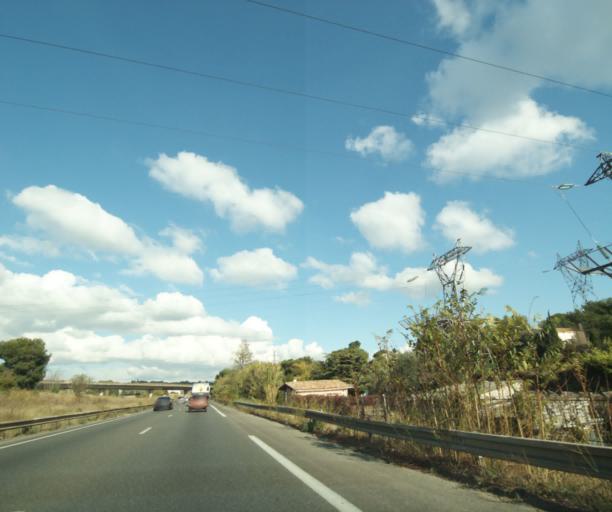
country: FR
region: Provence-Alpes-Cote d'Azur
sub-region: Departement des Bouches-du-Rhone
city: Septemes-les-Vallons
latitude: 43.3974
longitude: 5.3524
